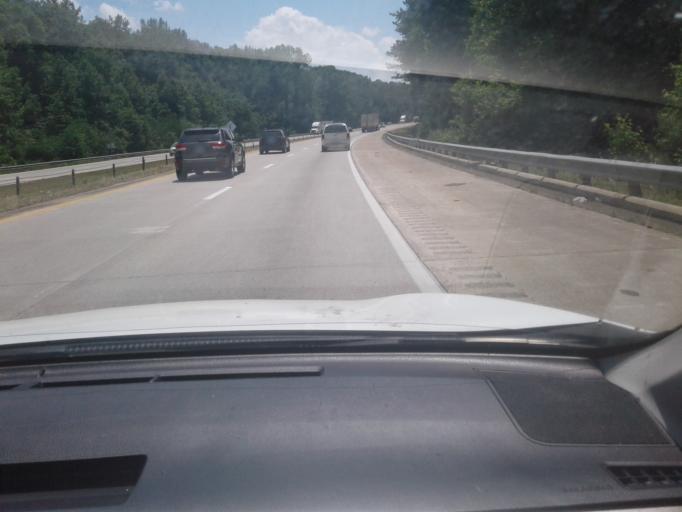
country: US
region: North Carolina
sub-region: Johnston County
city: Clayton
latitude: 35.5606
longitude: -78.5761
